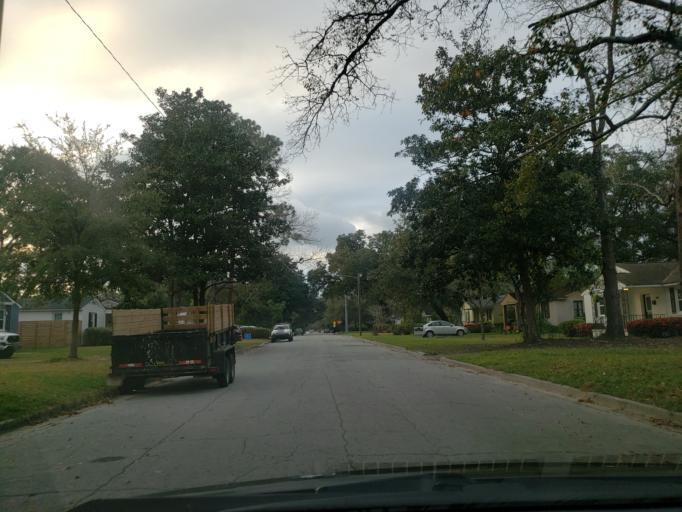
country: US
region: Georgia
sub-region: Chatham County
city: Thunderbolt
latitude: 32.0304
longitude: -81.0992
